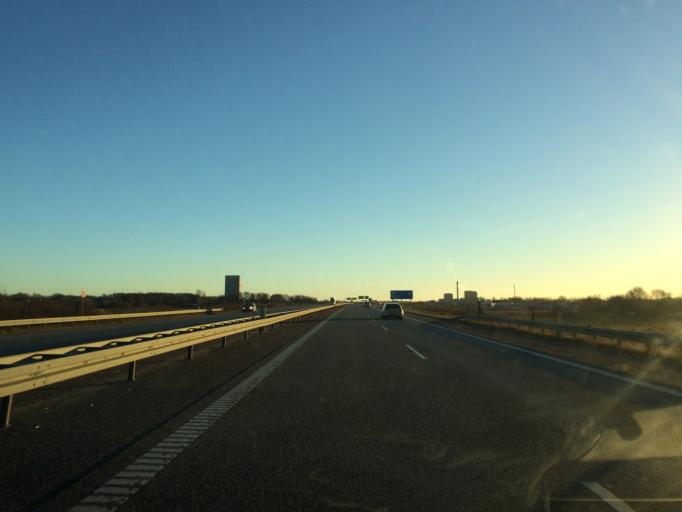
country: DK
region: Central Jutland
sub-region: Herning Kommune
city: Gjellerup Kirkeby
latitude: 56.1410
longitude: 9.0122
